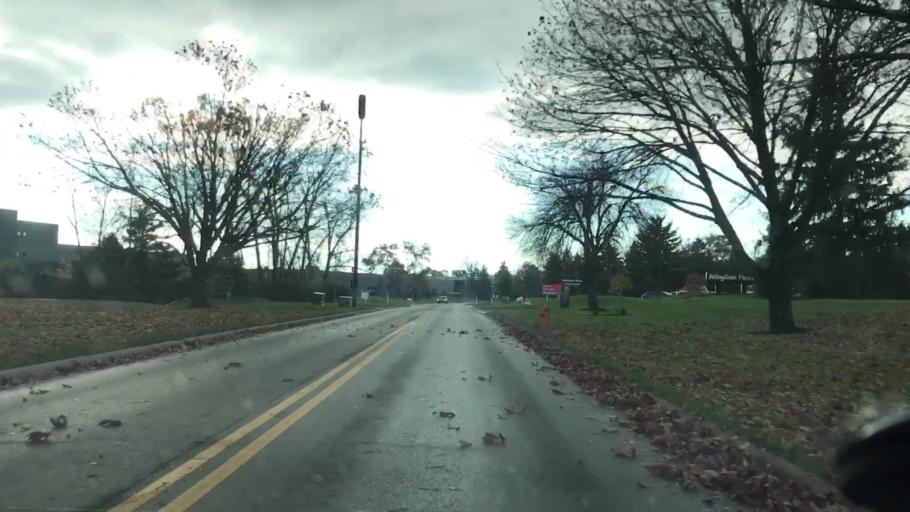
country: US
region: Ohio
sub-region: Franklin County
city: Lincoln Village
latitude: 39.9896
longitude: -83.1150
